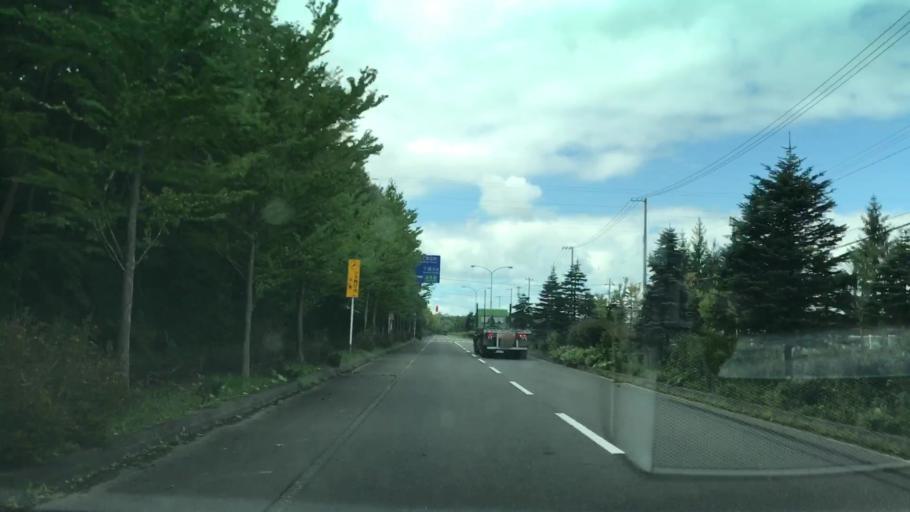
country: JP
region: Hokkaido
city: Chitose
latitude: 42.7726
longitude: 141.6183
